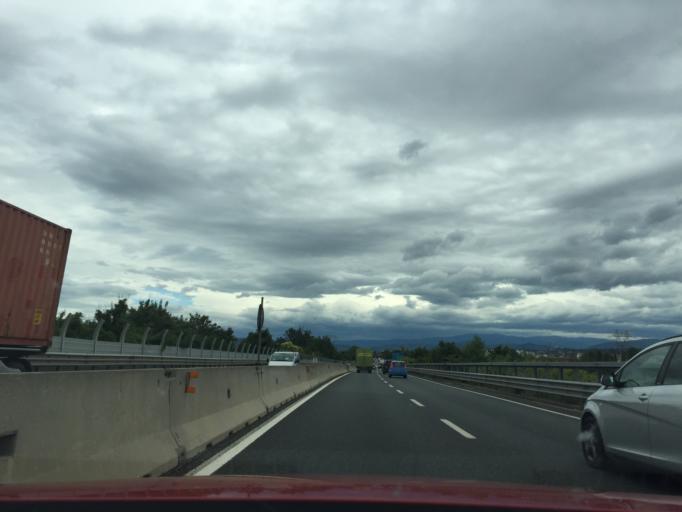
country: IT
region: Tuscany
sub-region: Province of Florence
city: San Donnino
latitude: 43.7739
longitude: 11.1419
